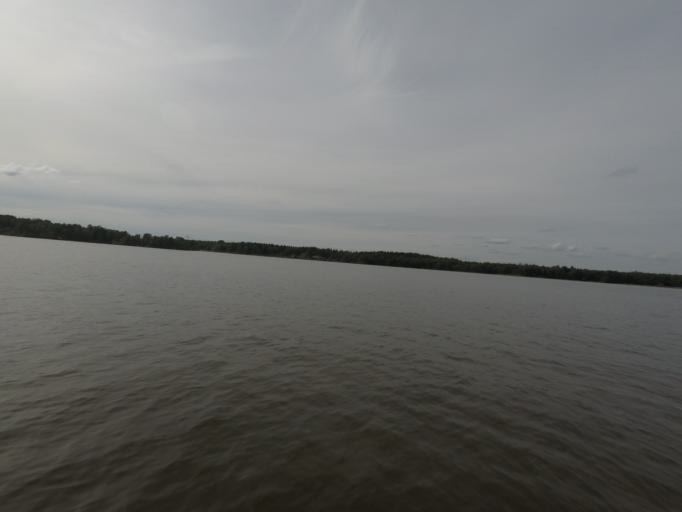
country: SE
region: Soedermanland
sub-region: Eskilstuna Kommun
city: Torshalla
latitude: 59.4772
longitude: 16.4676
